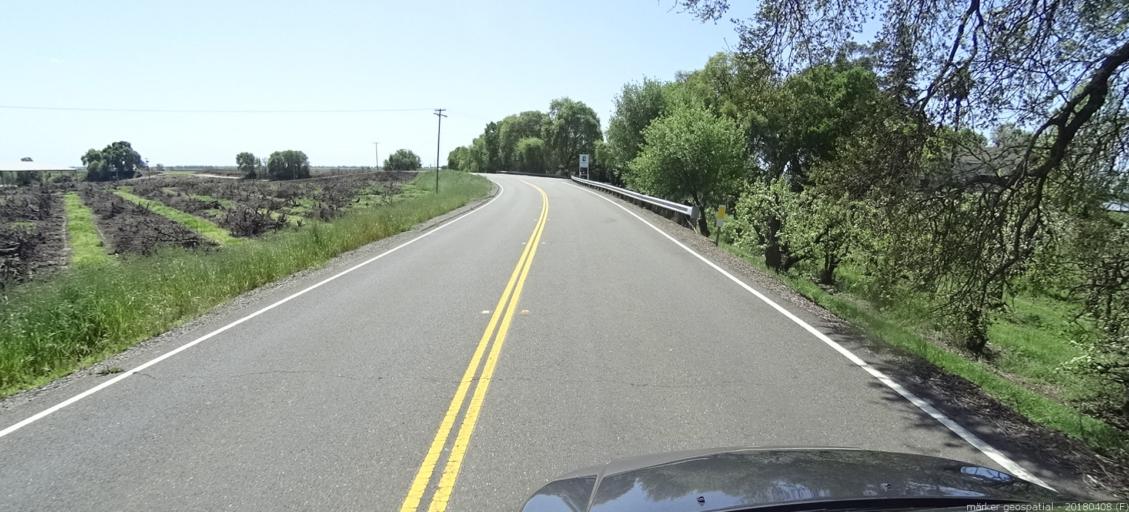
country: US
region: California
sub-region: Sacramento County
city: Walnut Grove
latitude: 38.3476
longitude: -121.5355
